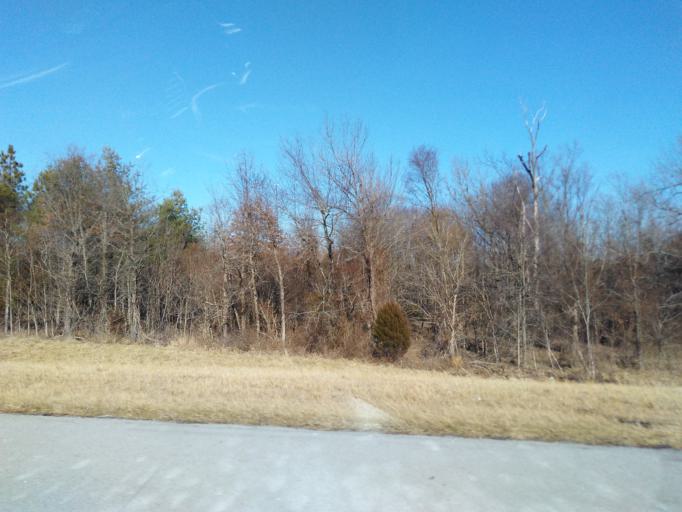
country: US
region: Illinois
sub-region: Johnson County
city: Vienna
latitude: 37.3609
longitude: -88.7959
